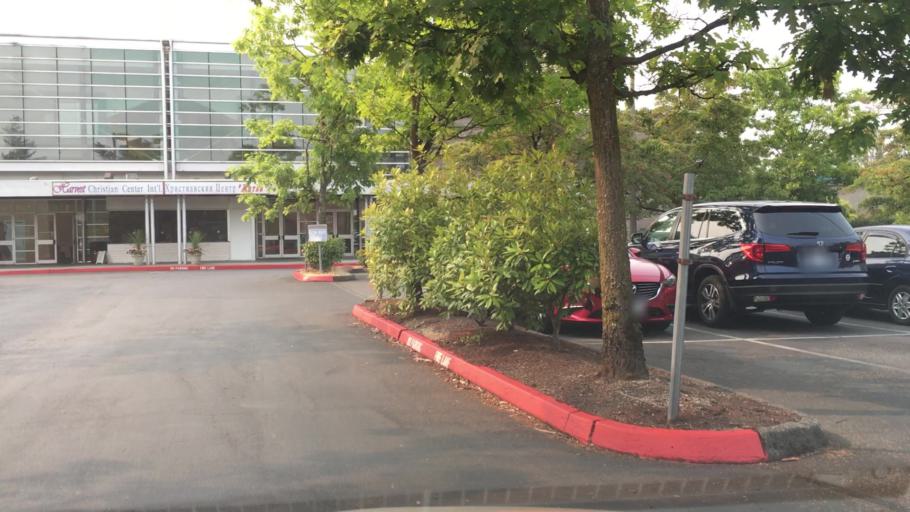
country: US
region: Washington
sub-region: Snohomish County
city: Mill Creek
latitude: 47.9093
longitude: -122.2211
